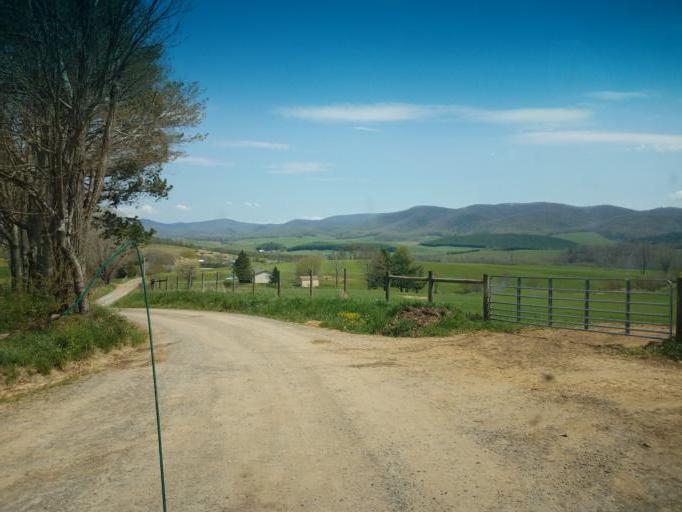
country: US
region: Virginia
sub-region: Smyth County
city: Marion
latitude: 36.7800
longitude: -81.4616
